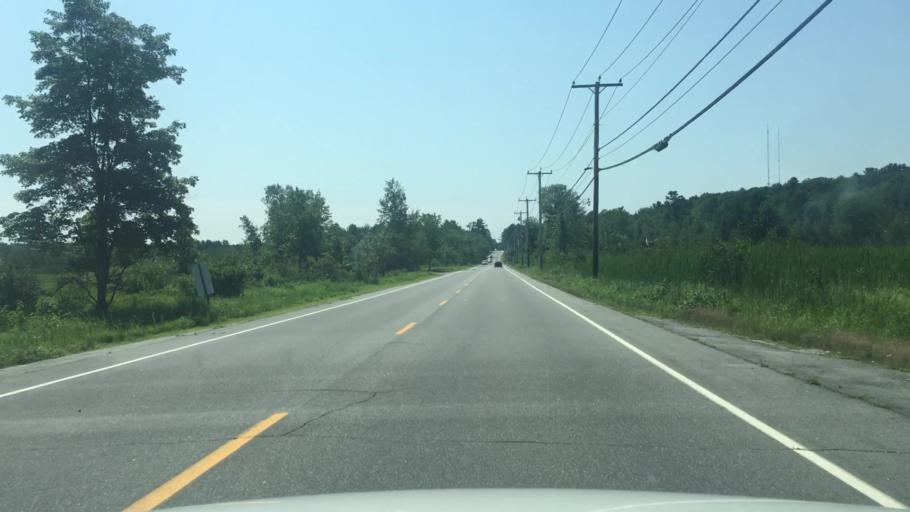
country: US
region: Maine
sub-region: Cumberland County
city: Cumberland Center
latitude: 43.8706
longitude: -70.3259
